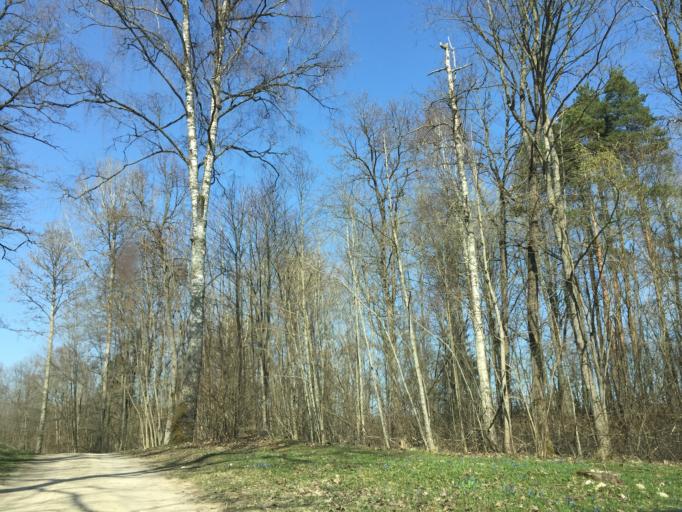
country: LV
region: Malpils
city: Malpils
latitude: 57.0070
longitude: 24.9721
